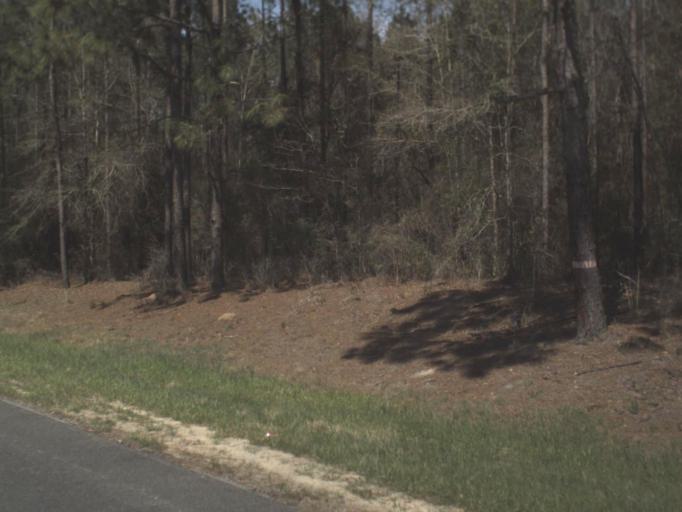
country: US
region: Florida
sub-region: Holmes County
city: Bonifay
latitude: 30.7945
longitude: -85.7286
